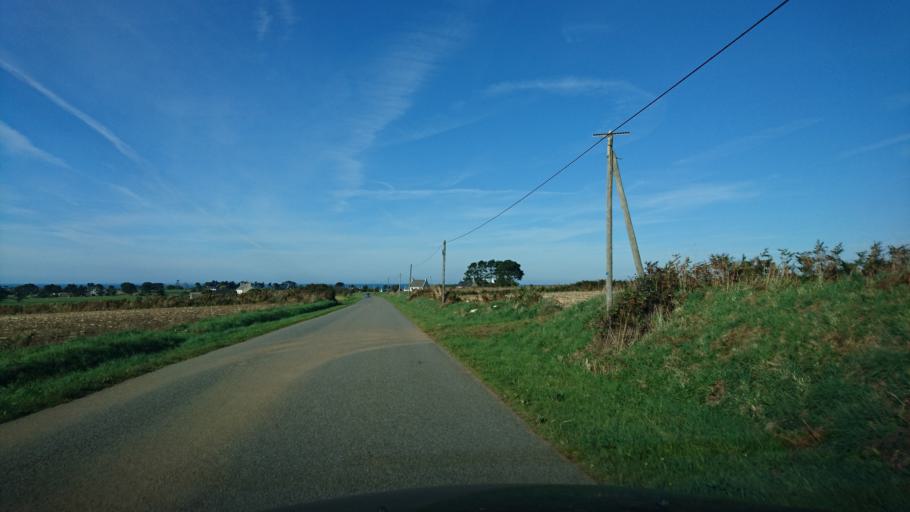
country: FR
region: Brittany
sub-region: Departement du Finistere
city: Lampaul-Plouarzel
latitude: 48.4286
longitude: -4.7550
